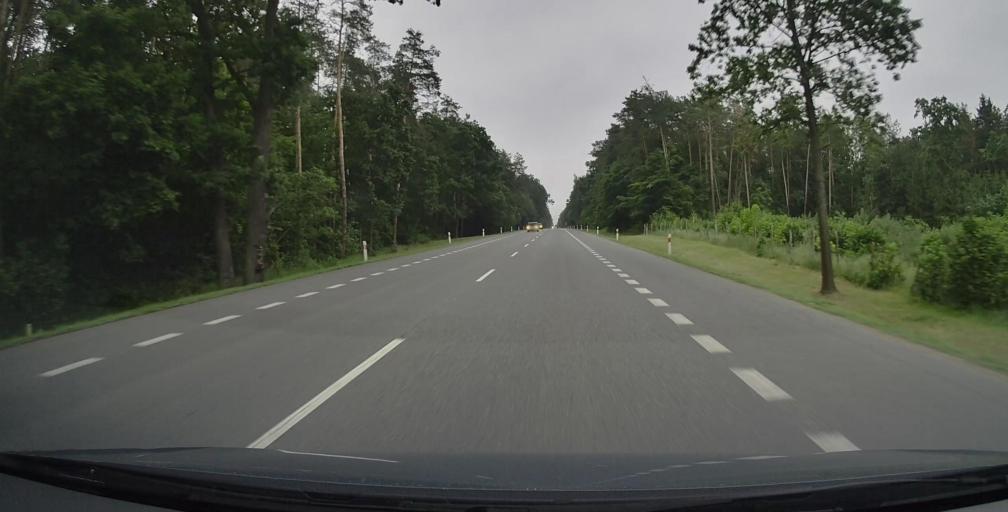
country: PL
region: Lublin Voivodeship
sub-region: Powiat bialski
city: Zalesie
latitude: 52.0362
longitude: 23.4151
